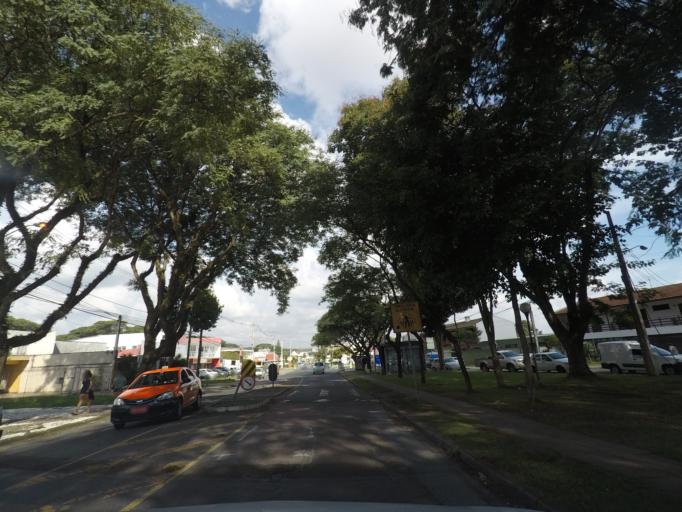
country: BR
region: Parana
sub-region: Pinhais
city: Pinhais
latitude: -25.4568
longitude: -49.2256
